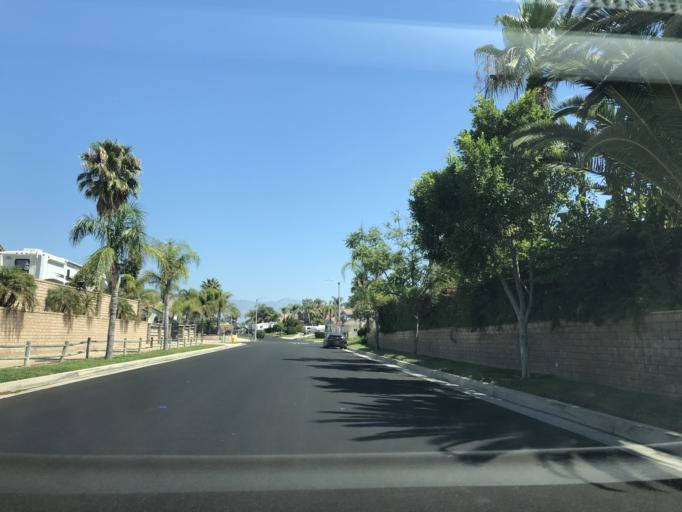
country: US
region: California
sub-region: Riverside County
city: Norco
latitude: 33.9144
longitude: -117.5790
